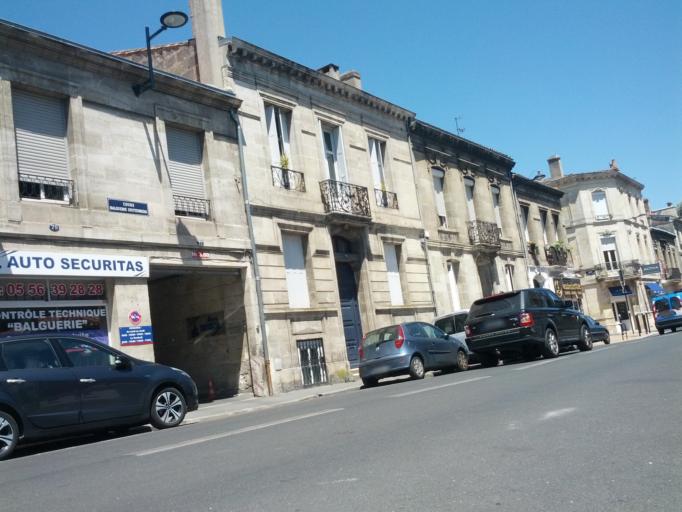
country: FR
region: Aquitaine
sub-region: Departement de la Gironde
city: Bordeaux
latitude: 44.8577
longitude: -0.5677
